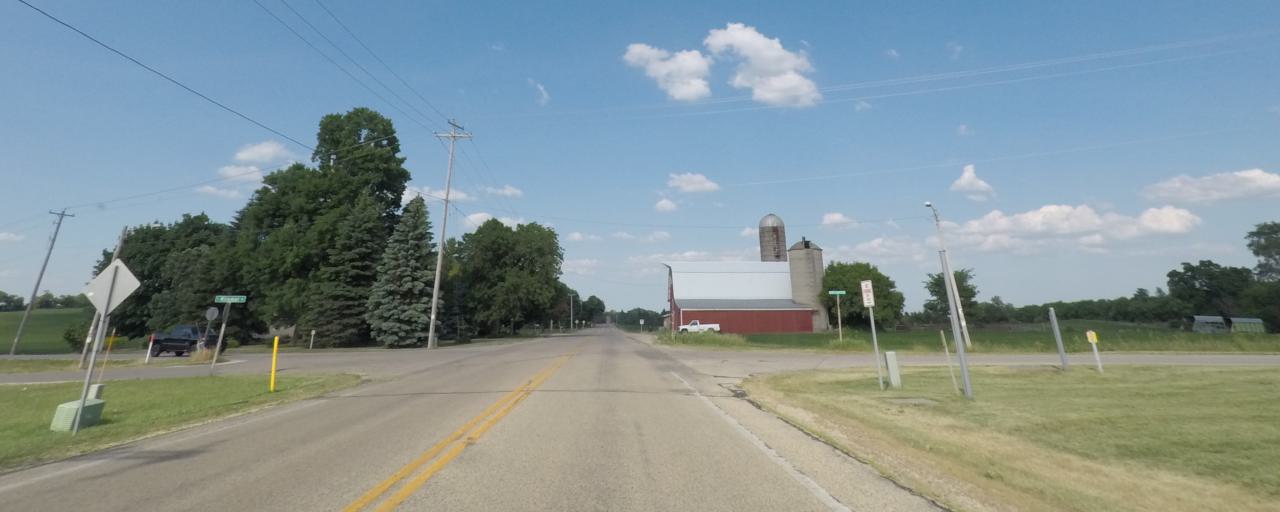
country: US
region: Wisconsin
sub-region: Walworth County
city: Potter Lake
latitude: 42.8150
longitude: -88.3369
